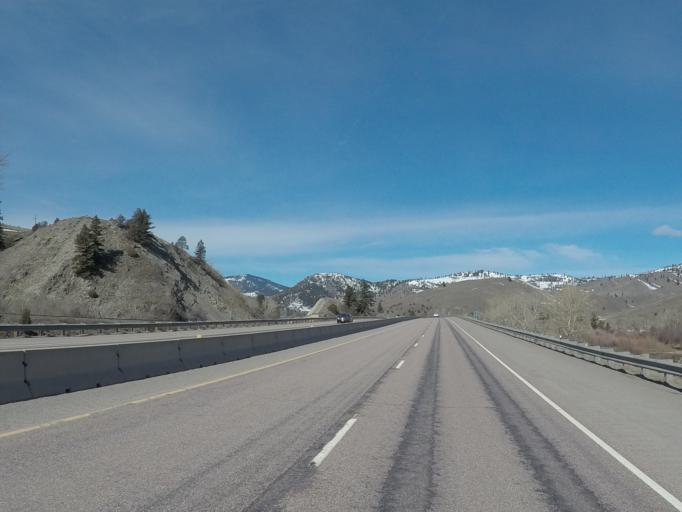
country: US
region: Montana
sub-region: Granite County
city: Philipsburg
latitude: 46.7109
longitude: -113.2648
